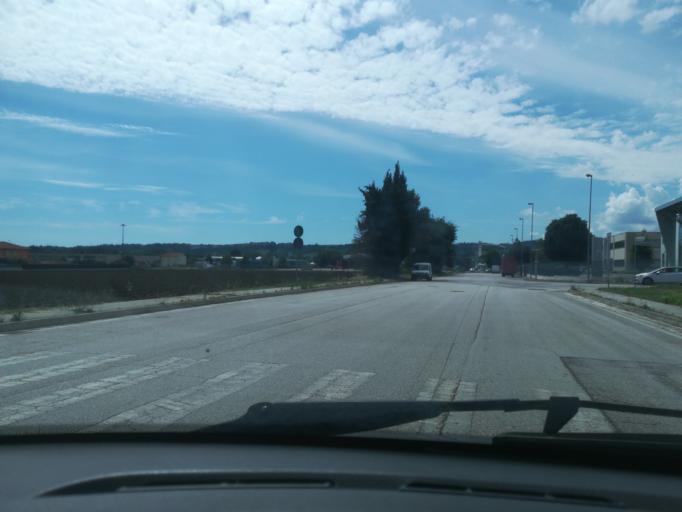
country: IT
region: The Marches
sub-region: Provincia di Macerata
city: Santa Maria Apparente
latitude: 43.2847
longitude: 13.6807
